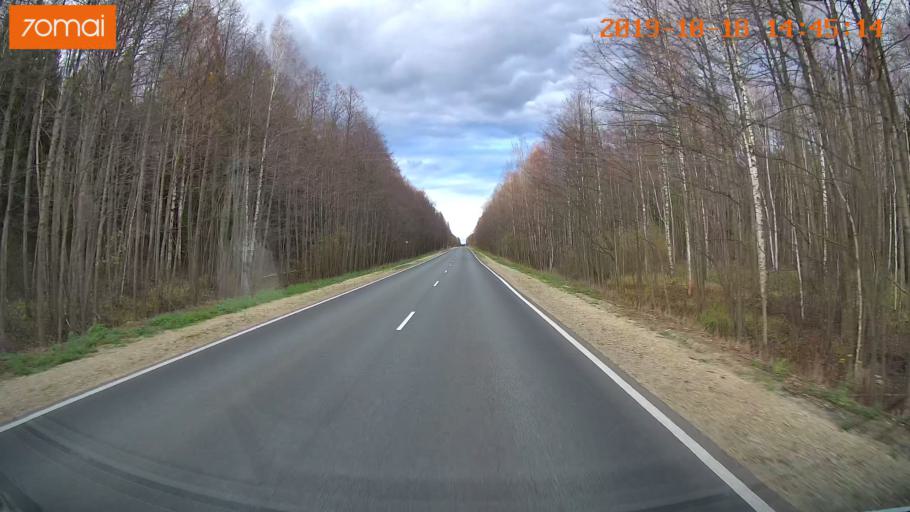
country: RU
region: Vladimir
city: Velikodvorskiy
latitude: 55.3515
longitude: 40.6785
